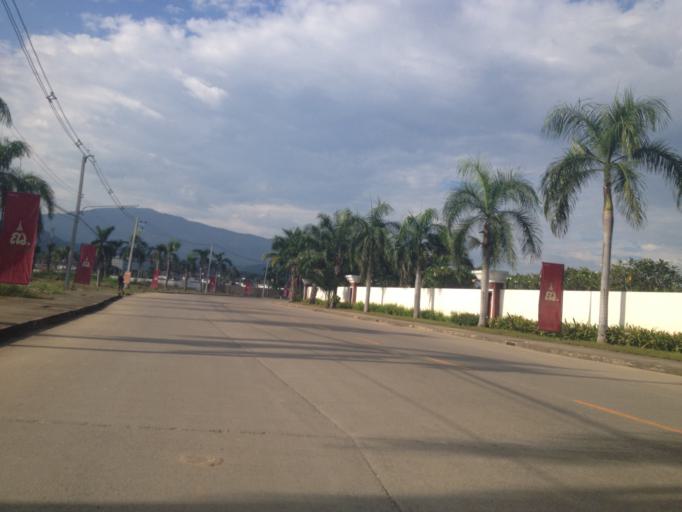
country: TH
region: Chiang Mai
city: Hang Dong
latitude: 18.7189
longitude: 98.9147
